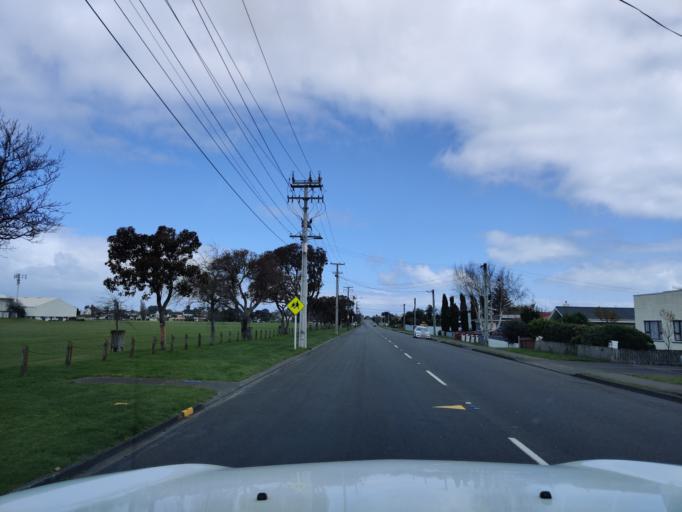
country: NZ
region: Manawatu-Wanganui
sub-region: Wanganui District
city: Wanganui
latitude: -39.9271
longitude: 175.0297
